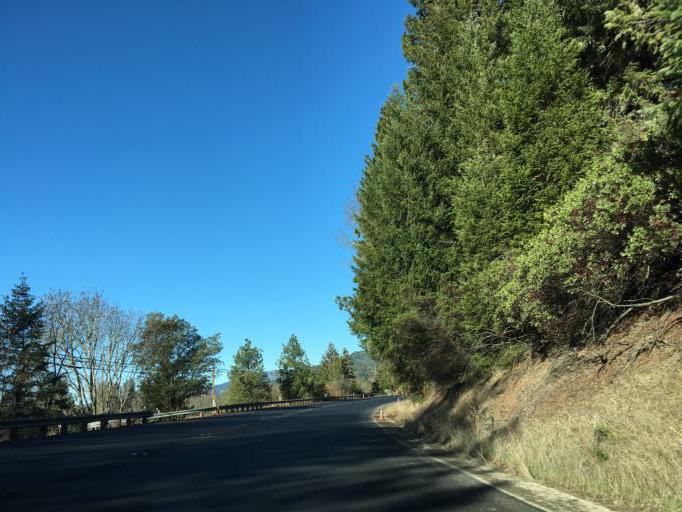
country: US
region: California
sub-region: Mendocino County
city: Laytonville
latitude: 39.6590
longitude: -123.4777
